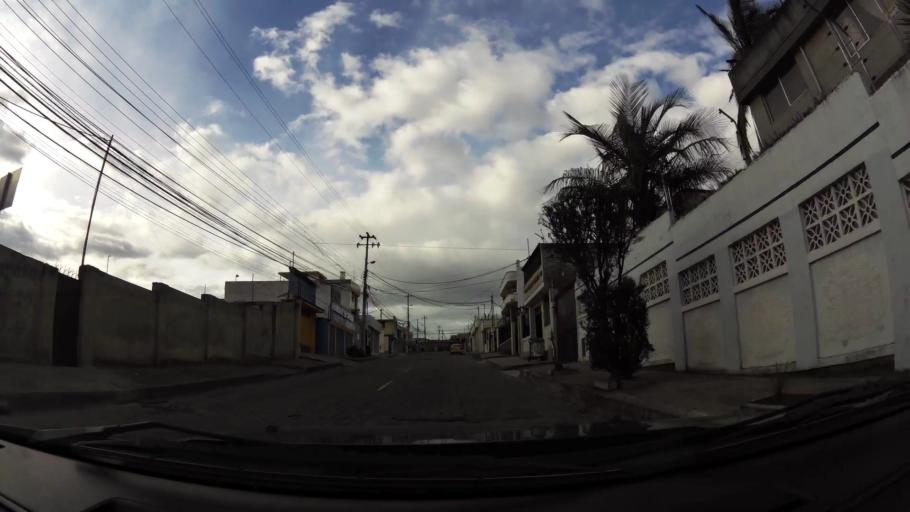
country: EC
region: Pichincha
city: Quito
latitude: -0.1482
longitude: -78.4707
